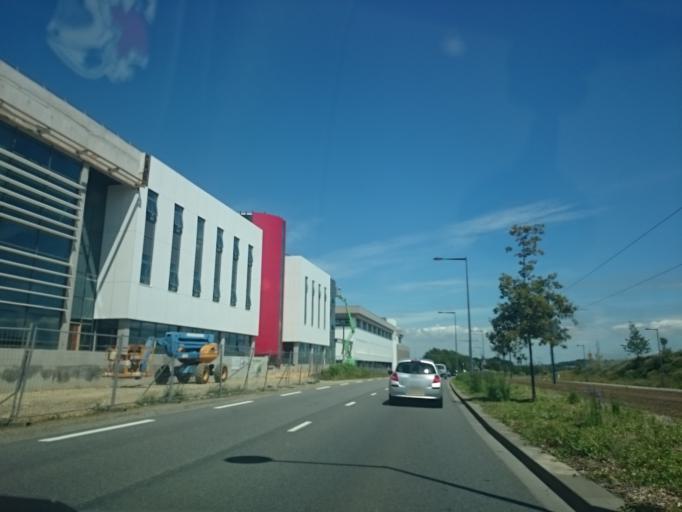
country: FR
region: Brittany
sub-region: Departement du Finistere
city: Gouesnou
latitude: 48.4190
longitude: -4.4515
